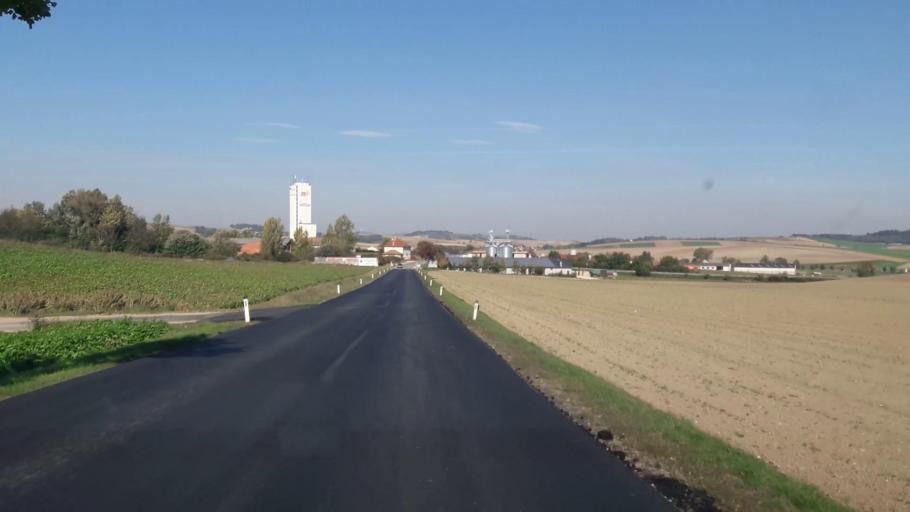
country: AT
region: Lower Austria
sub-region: Politischer Bezirk Korneuburg
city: Grossrussbach
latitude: 48.4704
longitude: 16.3795
